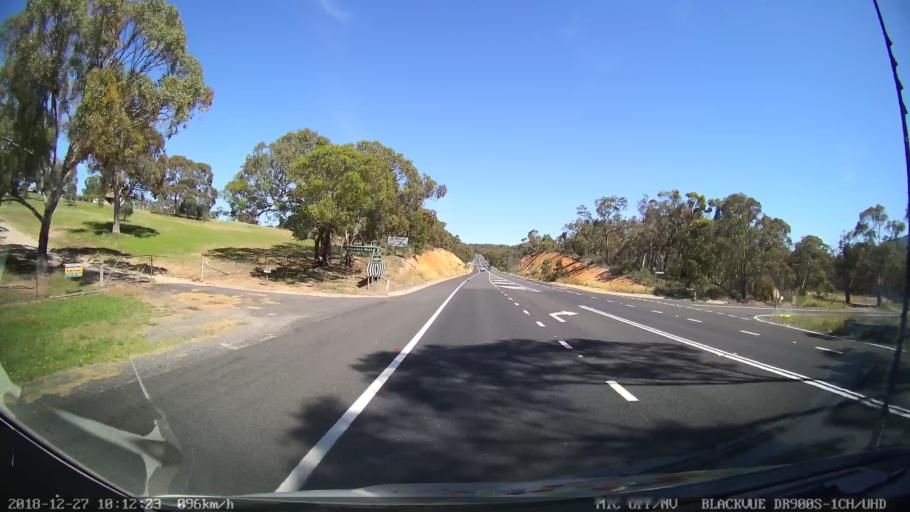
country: AU
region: New South Wales
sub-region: Bathurst Regional
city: Kelso
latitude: -33.4438
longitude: 149.7611
